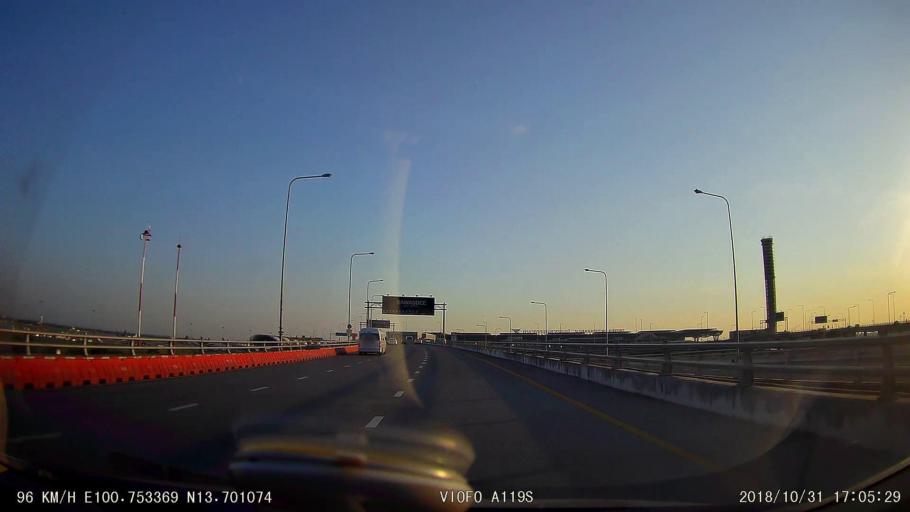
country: TH
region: Bangkok
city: Lat Krabang
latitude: 13.7007
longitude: 100.7533
